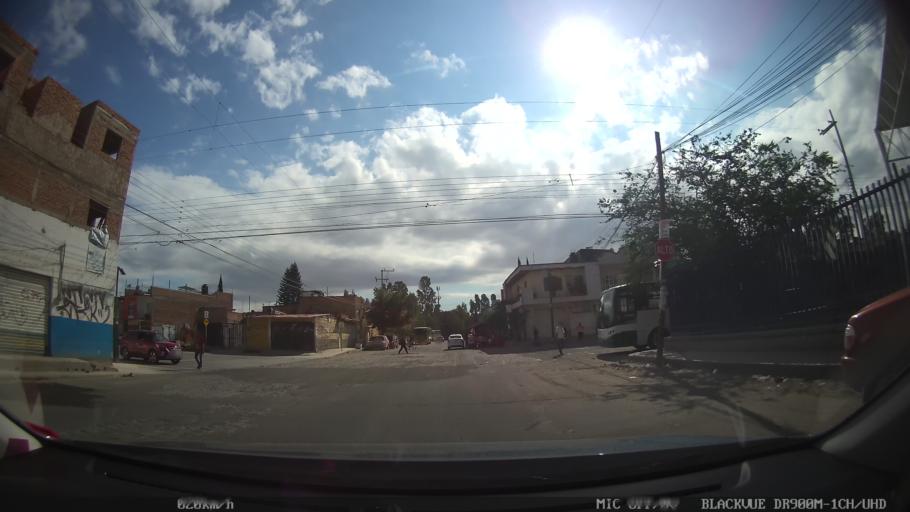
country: MX
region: Jalisco
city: Tonala
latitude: 20.6540
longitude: -103.2477
